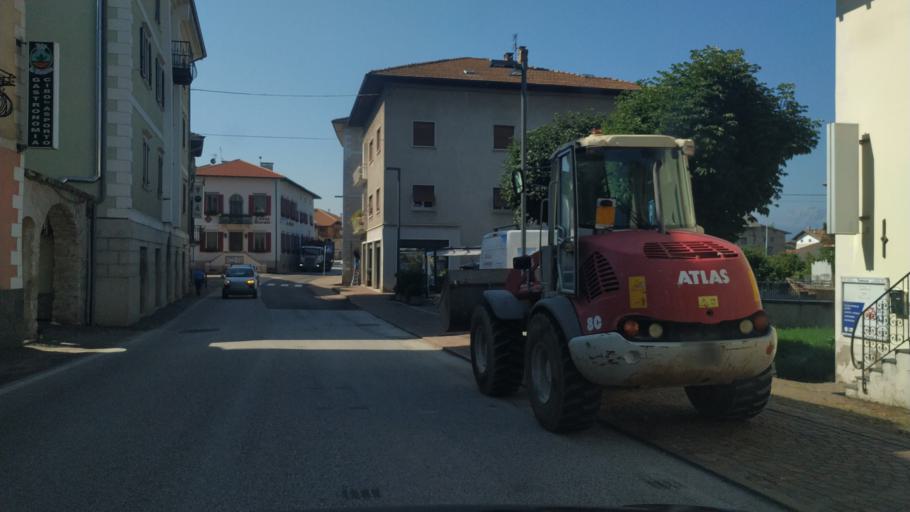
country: IT
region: Trentino-Alto Adige
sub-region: Provincia di Trento
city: Cavareno
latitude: 46.4101
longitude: 11.1376
